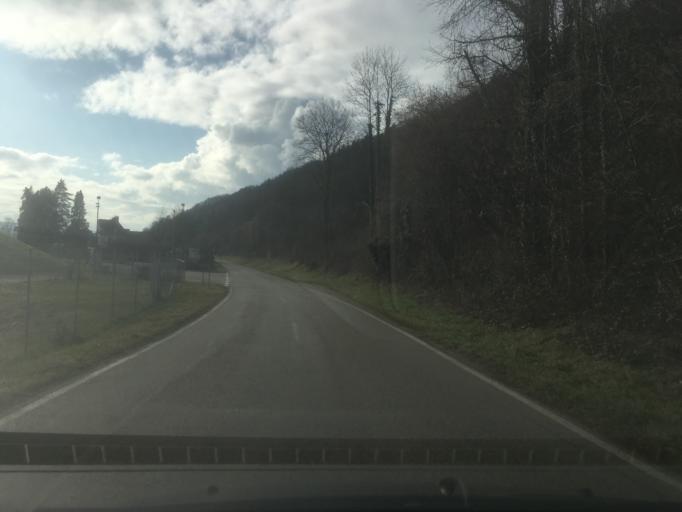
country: CH
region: Aargau
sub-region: Bezirk Zurzach
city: Koblenz
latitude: 47.6206
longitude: 8.2426
